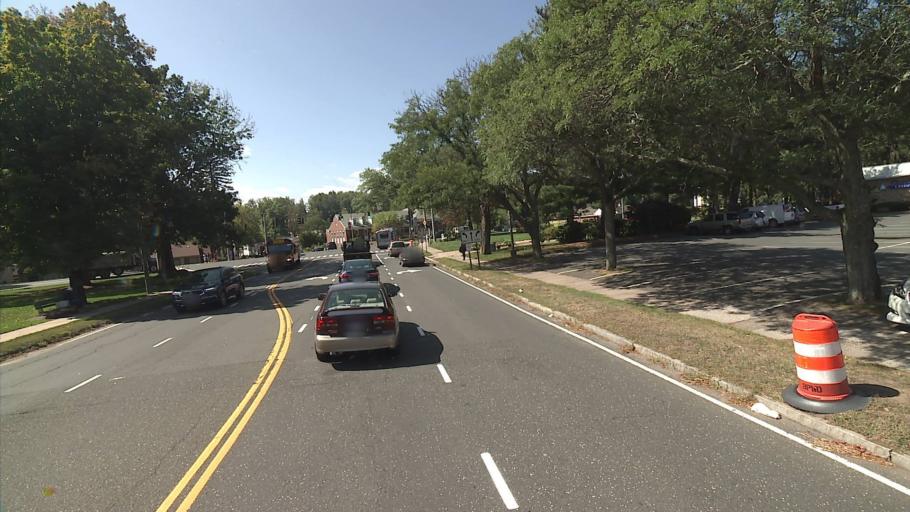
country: US
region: Connecticut
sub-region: Hartford County
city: Blue Hills
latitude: 41.8306
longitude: -72.7366
